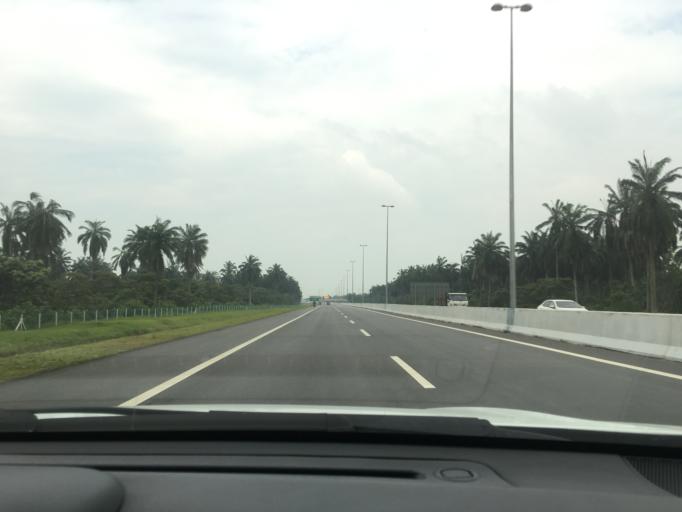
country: MY
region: Selangor
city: Klang
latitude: 3.1200
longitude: 101.4088
